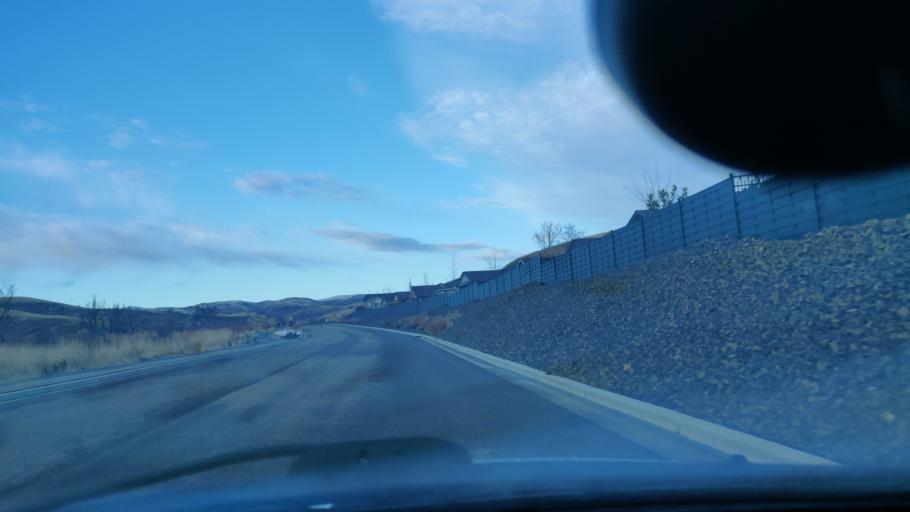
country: US
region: Idaho
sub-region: Ada County
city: Eagle
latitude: 43.7787
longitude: -116.2623
